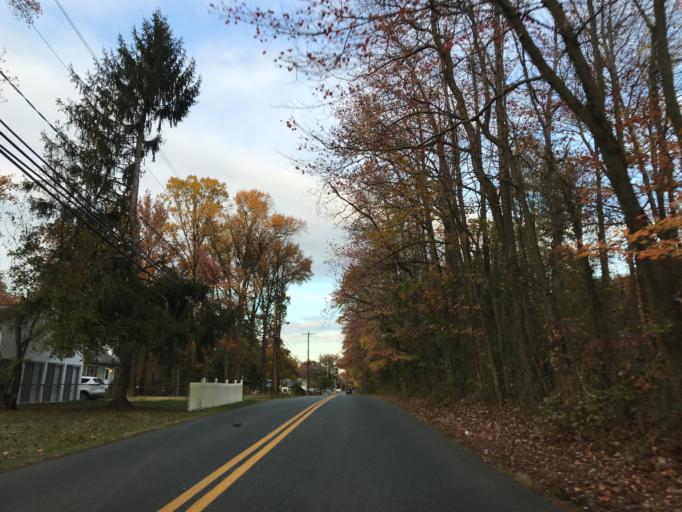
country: US
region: Maryland
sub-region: Baltimore County
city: Bowleys Quarters
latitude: 39.3703
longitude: -76.3624
